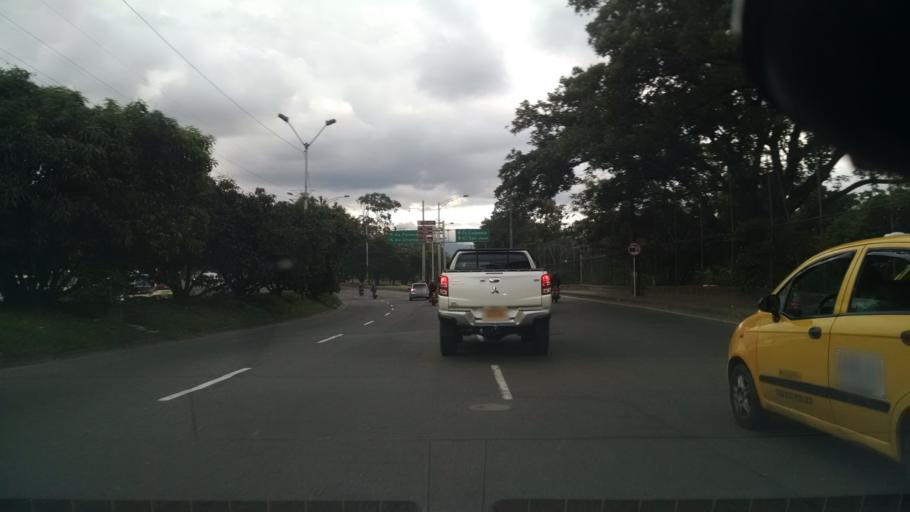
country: CO
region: Antioquia
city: Medellin
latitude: 6.2637
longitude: -75.5751
